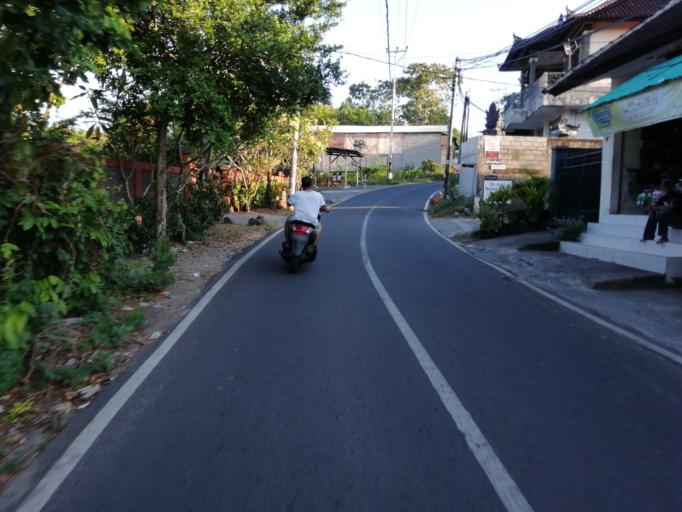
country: ID
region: Bali
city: Bualu
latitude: -8.7944
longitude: 115.1930
